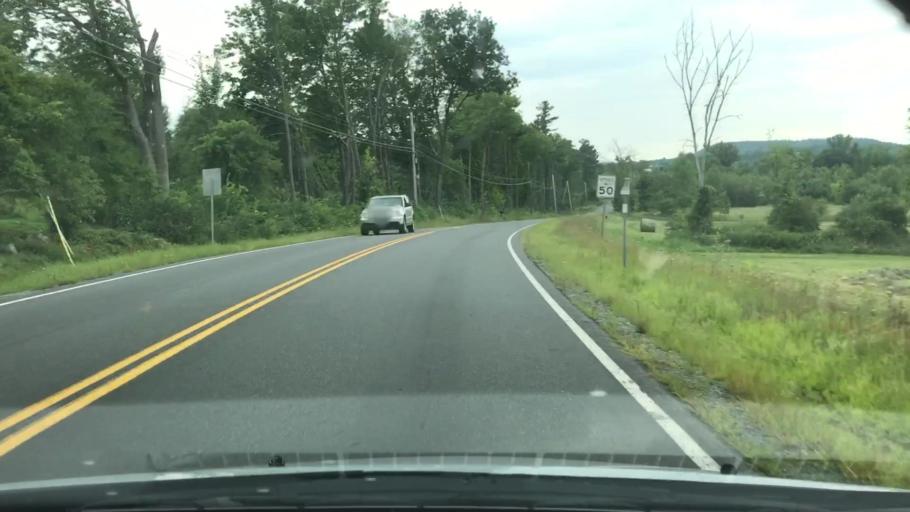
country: US
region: New Hampshire
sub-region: Grafton County
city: Haverhill
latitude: 44.0155
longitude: -72.0679
